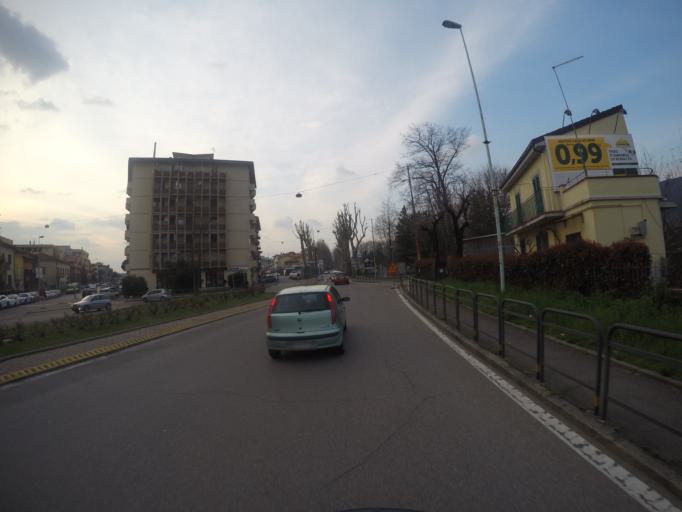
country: IT
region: Tuscany
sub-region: Provincia di Prato
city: Prato
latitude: 43.8625
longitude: 11.1188
